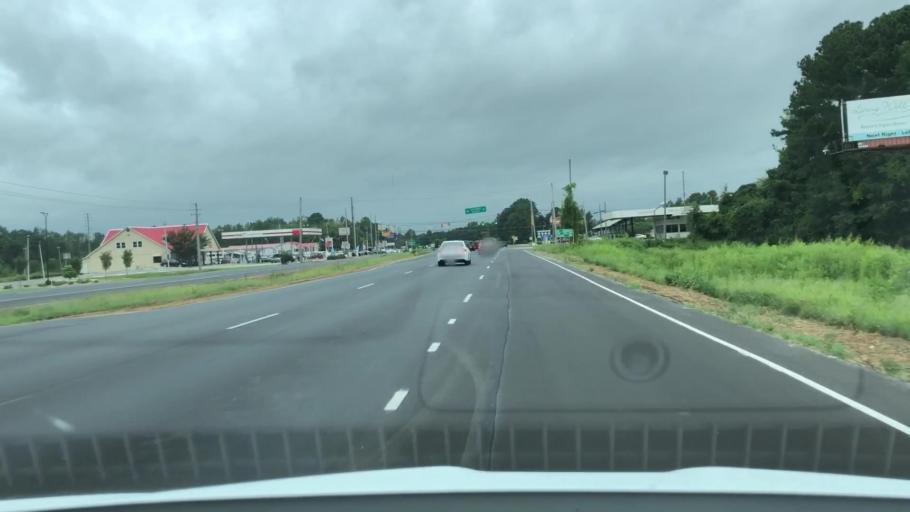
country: US
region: North Carolina
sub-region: Lenoir County
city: Kinston
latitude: 35.2532
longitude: -77.6000
